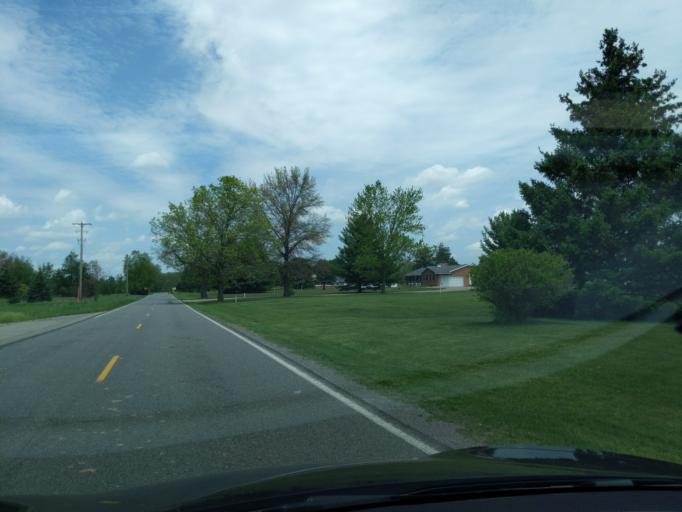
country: US
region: Michigan
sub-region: Ingham County
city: Stockbridge
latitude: 42.4572
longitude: -84.1654
